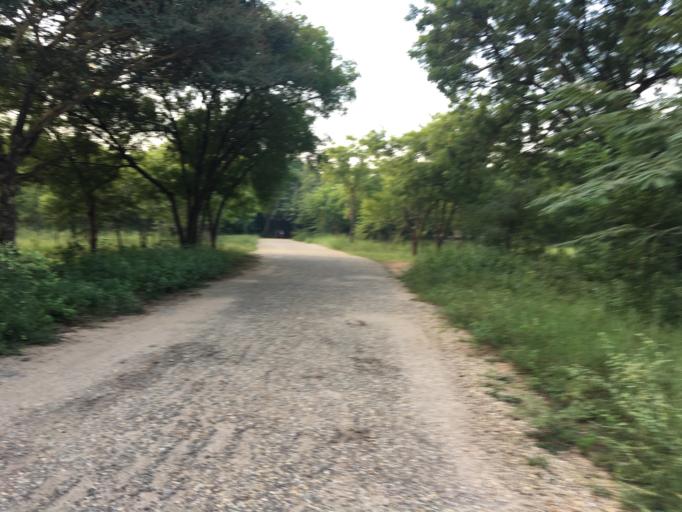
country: MM
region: Magway
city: Pakokku
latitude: 21.1800
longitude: 94.9048
